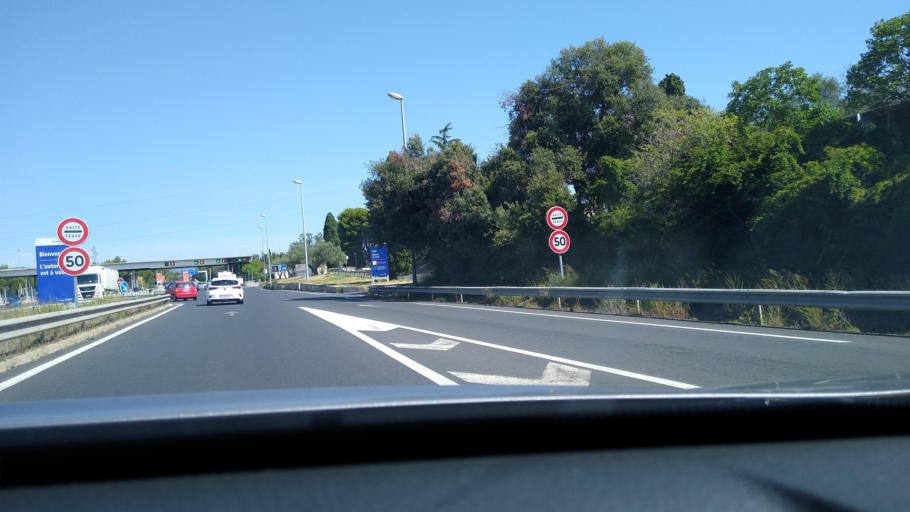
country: FR
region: Languedoc-Roussillon
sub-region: Departement de l'Herault
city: Balaruc-le-Vieux
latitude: 43.4761
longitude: 3.6858
